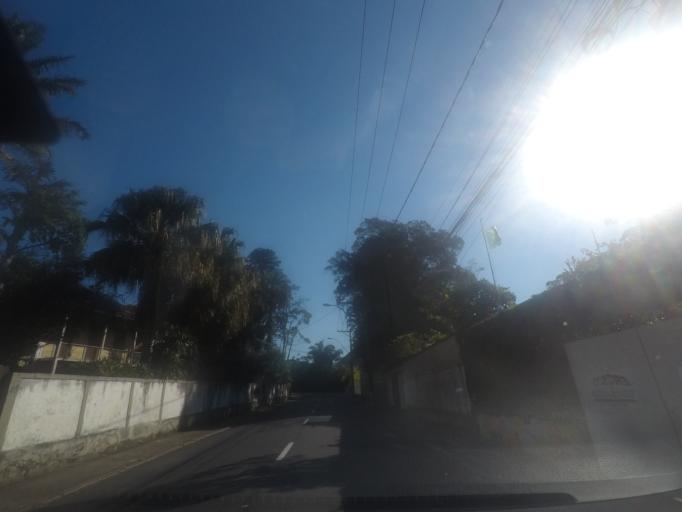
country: BR
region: Rio de Janeiro
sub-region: Petropolis
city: Petropolis
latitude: -22.5130
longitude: -43.1672
